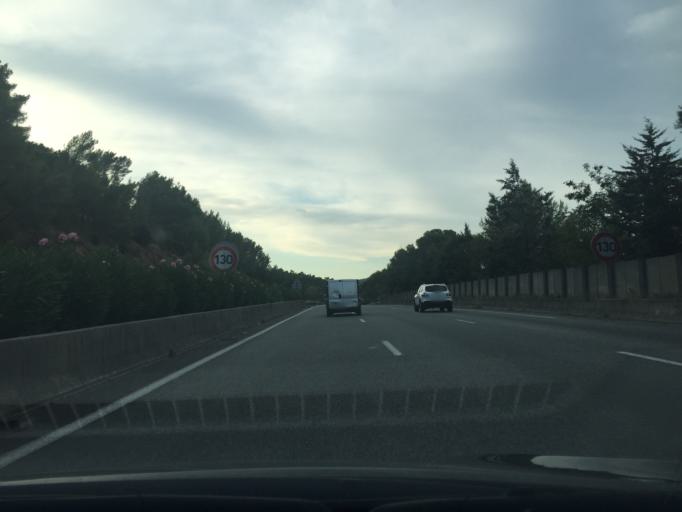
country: FR
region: Provence-Alpes-Cote d'Azur
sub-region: Departement du Var
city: Frejus
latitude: 43.4791
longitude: 6.7417
